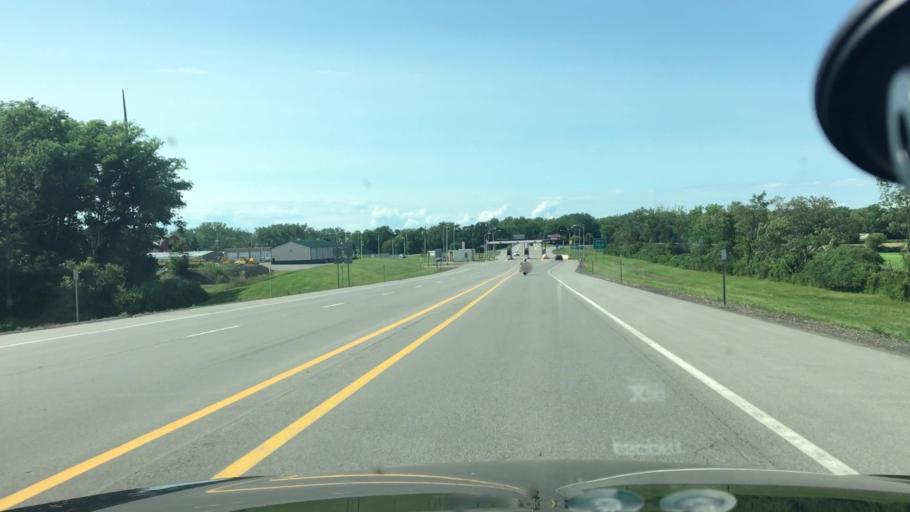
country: US
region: New York
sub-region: Chautauqua County
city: Silver Creek
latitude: 42.5578
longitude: -79.1142
